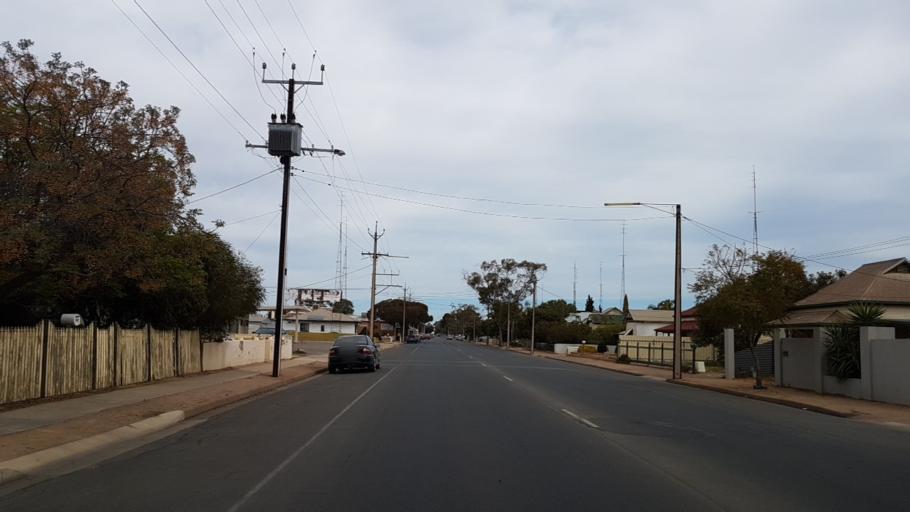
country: AU
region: South Australia
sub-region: Port Pirie City and Dists
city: Port Pirie
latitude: -33.1907
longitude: 138.0040
